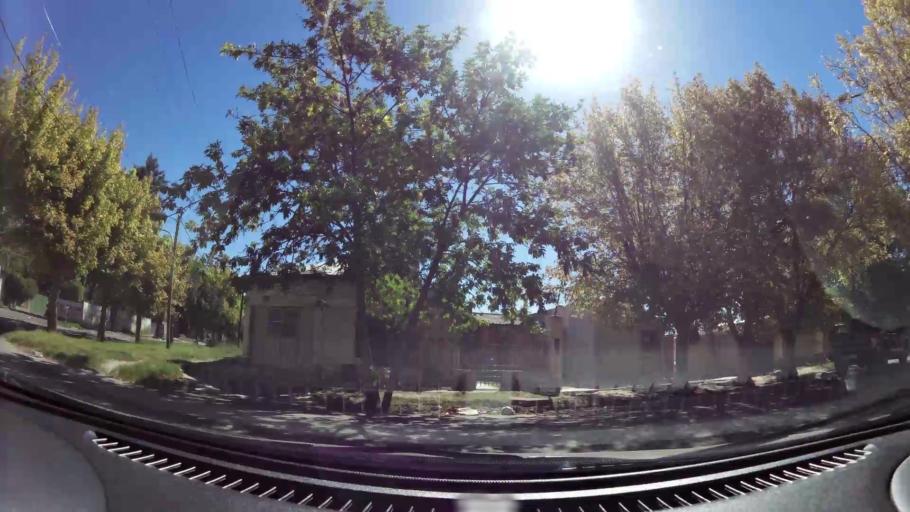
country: AR
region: Mendoza
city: Las Heras
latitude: -32.8323
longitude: -68.8236
